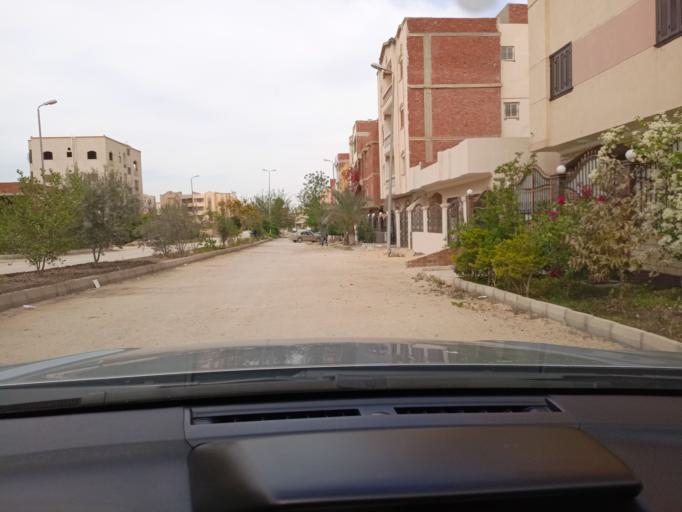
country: EG
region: Muhafazat al Qalyubiyah
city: Al Khankah
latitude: 30.2467
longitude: 31.4984
